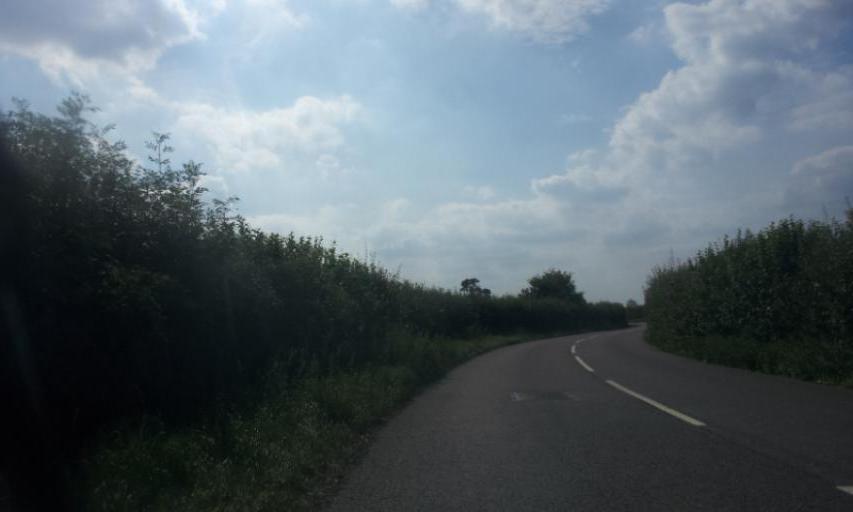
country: GB
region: England
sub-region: Kent
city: Marden
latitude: 51.1846
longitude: 0.4761
